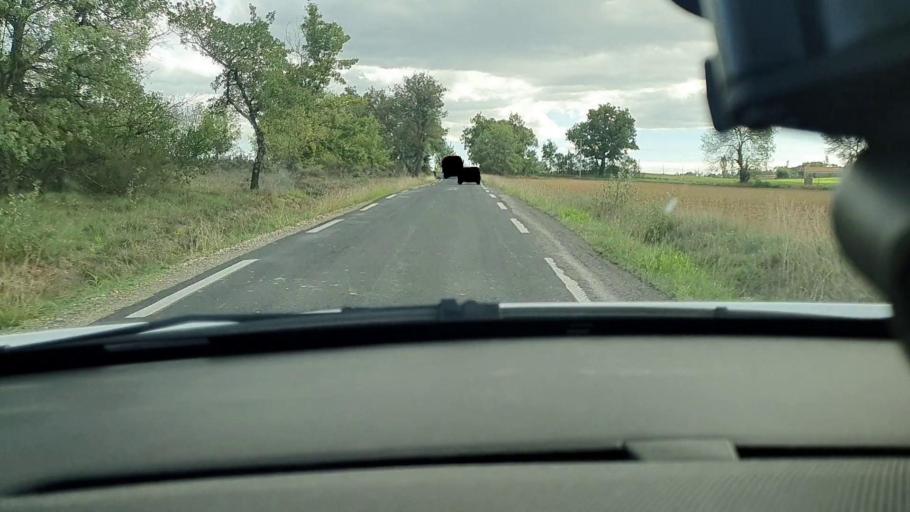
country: FR
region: Languedoc-Roussillon
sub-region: Departement du Gard
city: Les Mages
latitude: 44.1981
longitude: 4.2106
